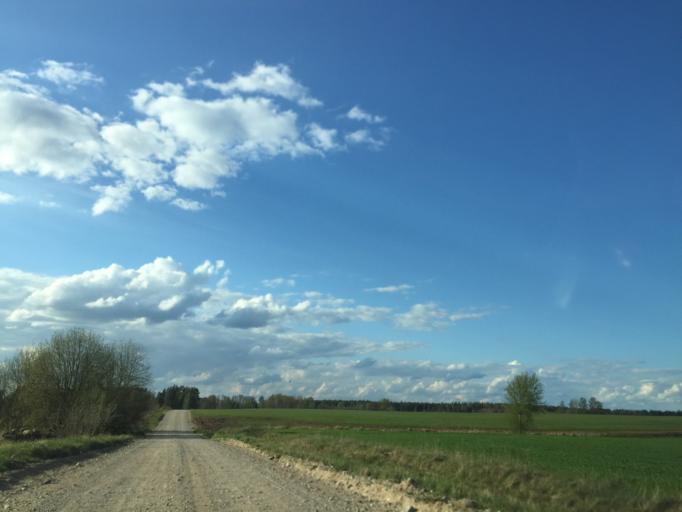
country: LV
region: Beverina
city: Murmuiza
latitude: 57.3867
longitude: 25.4837
